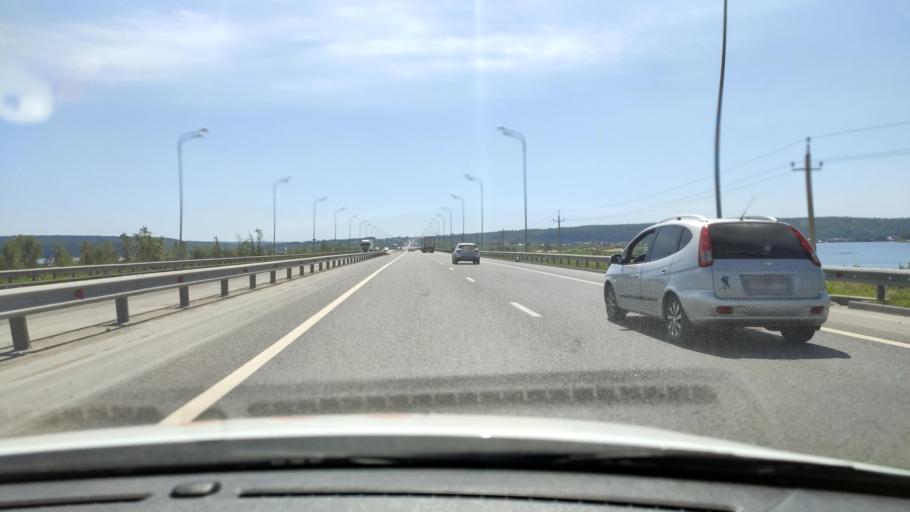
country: RU
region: Tatarstan
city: Osinovo
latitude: 55.8081
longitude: 48.8417
